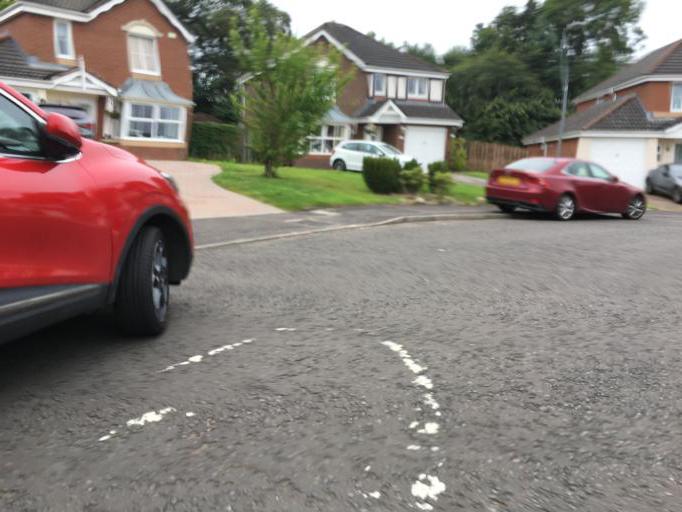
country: GB
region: Scotland
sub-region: West Lothian
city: Livingston
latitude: 55.8665
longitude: -3.5106
